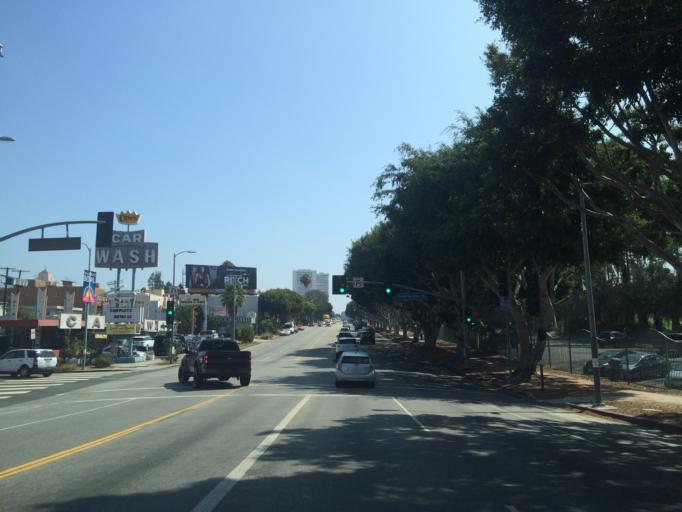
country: US
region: California
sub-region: Los Angeles County
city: Century City
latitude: 34.0460
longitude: -118.4174
